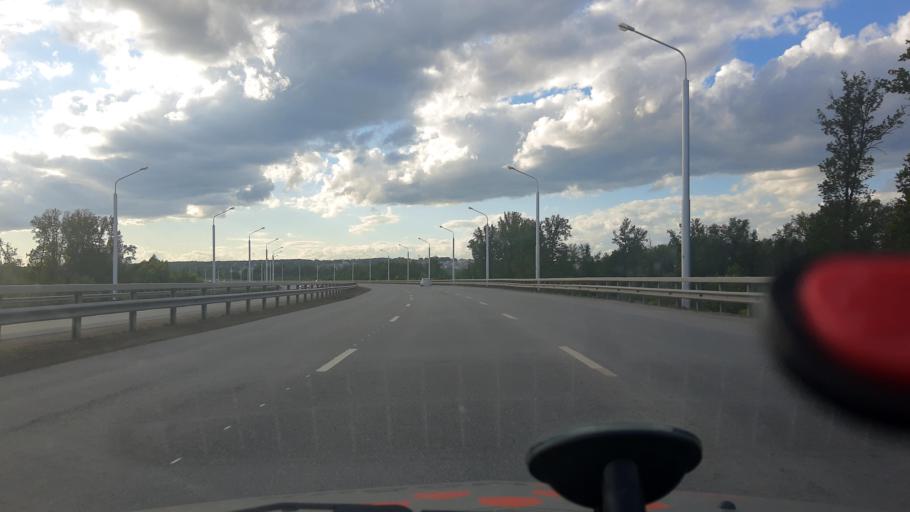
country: RU
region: Bashkortostan
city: Mikhaylovka
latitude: 54.7929
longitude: 55.9055
